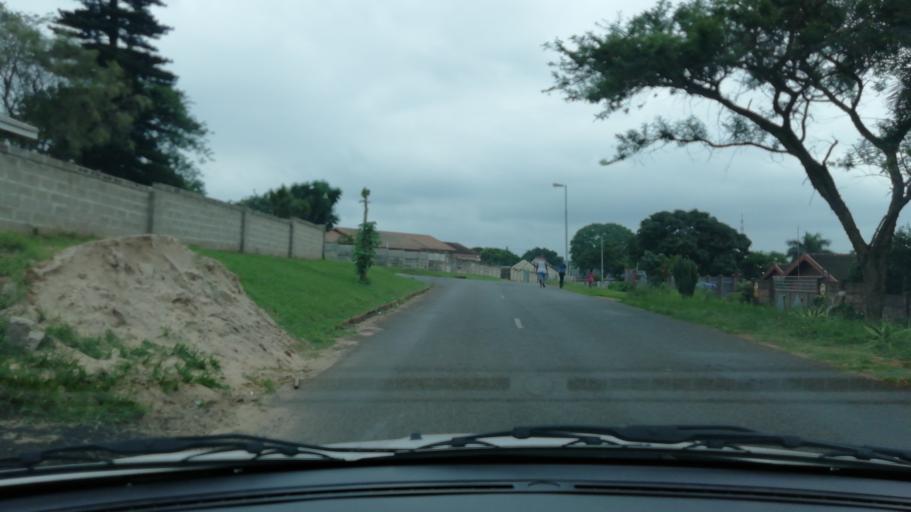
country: ZA
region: KwaZulu-Natal
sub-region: uThungulu District Municipality
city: Empangeni
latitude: -28.7371
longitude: 31.8986
